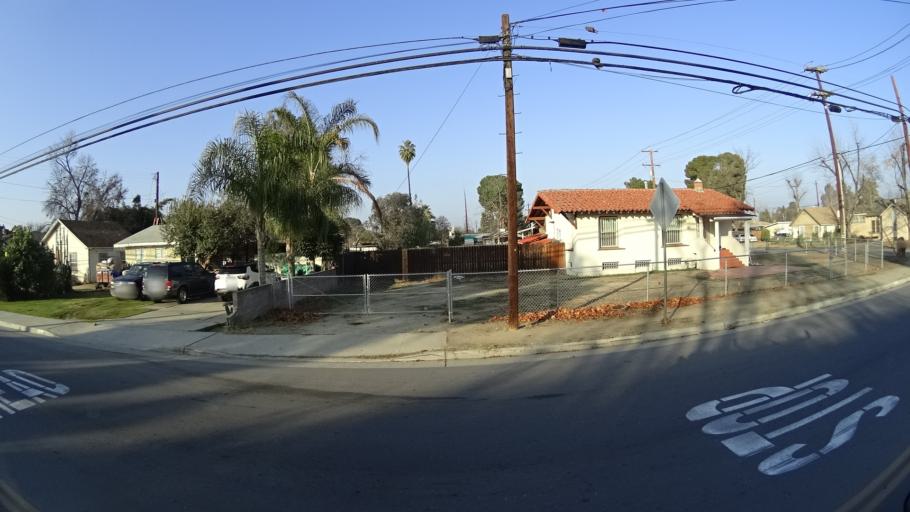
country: US
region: California
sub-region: Kern County
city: Bakersfield
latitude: 35.3621
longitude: -119.0435
